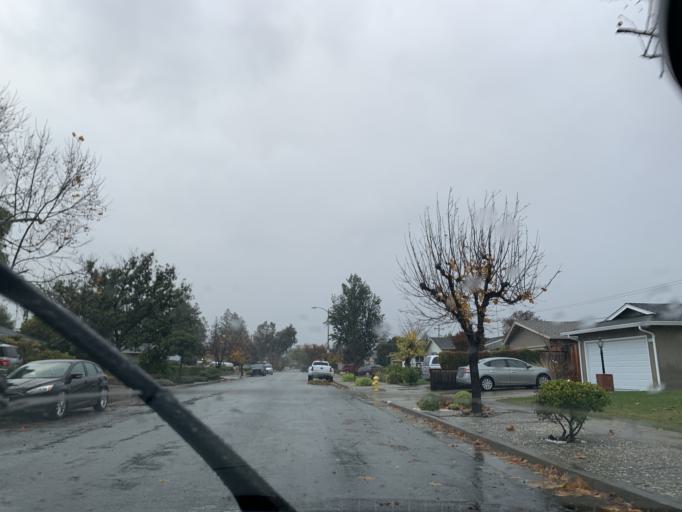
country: US
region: California
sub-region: Santa Clara County
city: Cambrian Park
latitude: 37.2582
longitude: -121.9416
